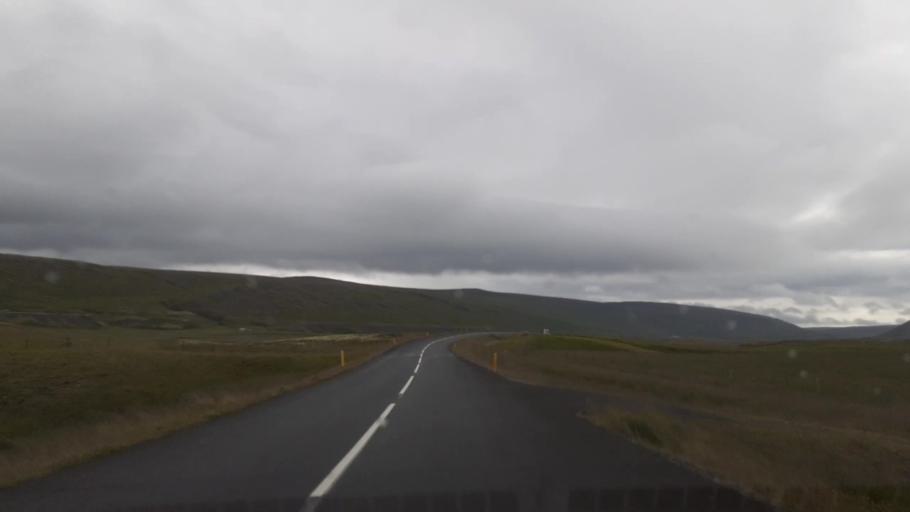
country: IS
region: East
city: Egilsstadir
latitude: 65.6338
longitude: -15.0570
